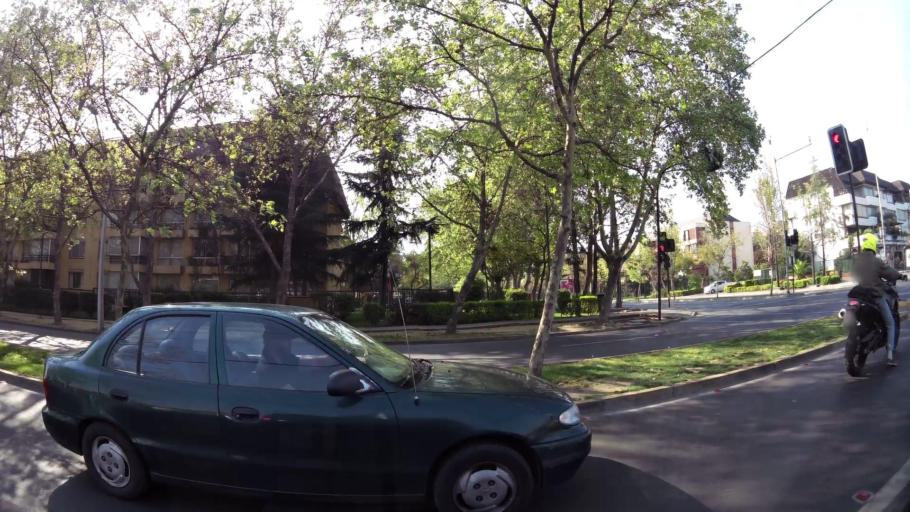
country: CL
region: Santiago Metropolitan
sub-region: Provincia de Santiago
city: Villa Presidente Frei, Nunoa, Santiago, Chile
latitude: -33.3838
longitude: -70.5513
